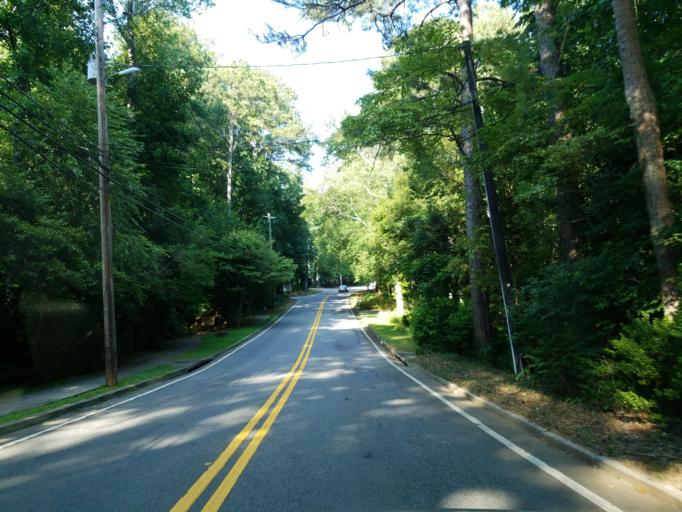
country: US
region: Georgia
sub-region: Fulton County
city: Roswell
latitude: 34.0030
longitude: -84.3406
